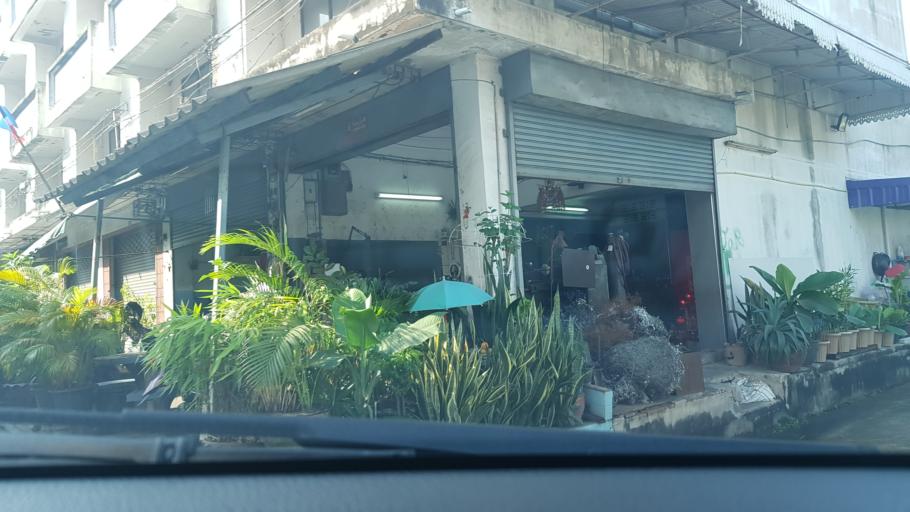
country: TH
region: Bangkok
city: Thawi Watthana
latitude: 13.7907
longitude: 100.3802
